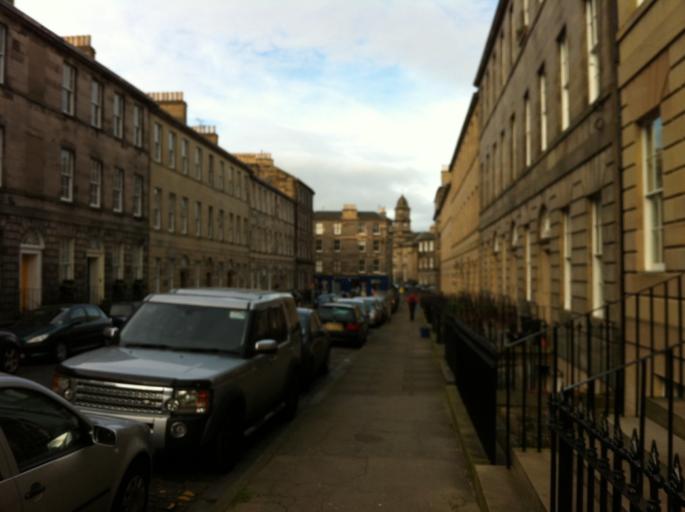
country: GB
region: Scotland
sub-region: Edinburgh
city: Edinburgh
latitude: 55.9589
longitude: -3.2056
